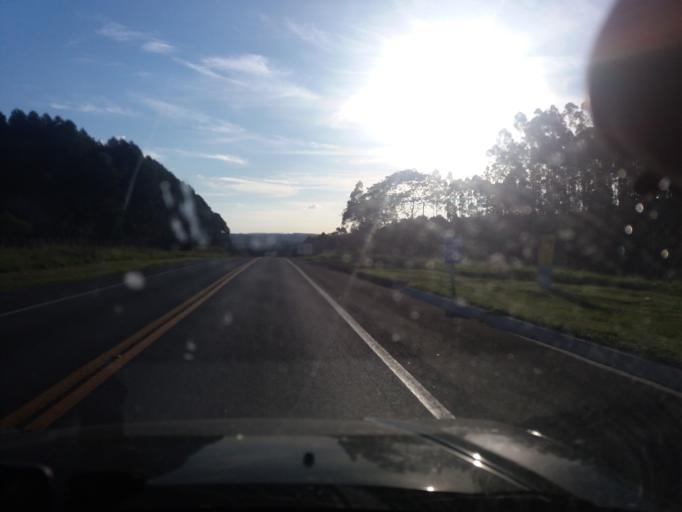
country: BR
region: Sao Paulo
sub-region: Buri
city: Buri
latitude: -23.9372
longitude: -48.6216
